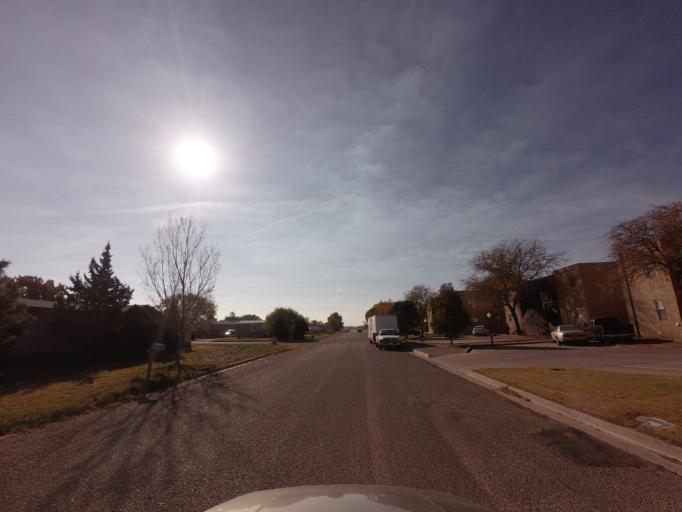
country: US
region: New Mexico
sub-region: Curry County
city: Clovis
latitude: 34.4078
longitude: -103.1752
